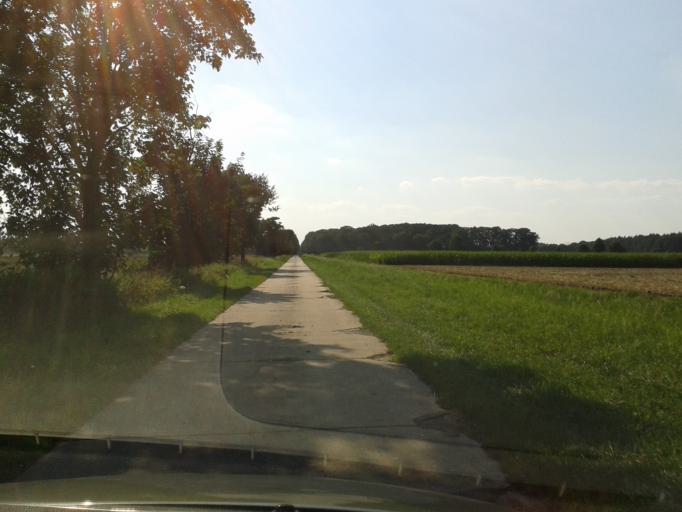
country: DE
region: Lower Saxony
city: Woltersdorf
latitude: 52.9100
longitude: 11.2287
